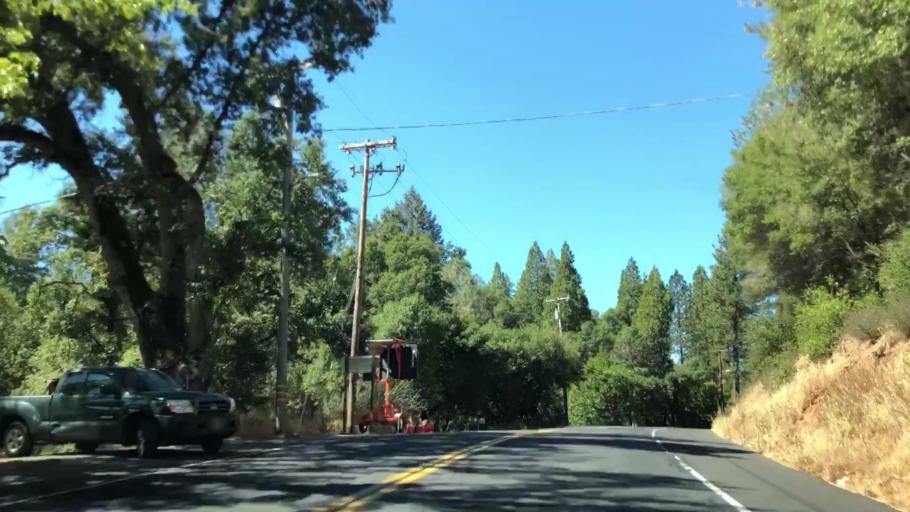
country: US
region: California
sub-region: Tuolumne County
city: Tuolumne City
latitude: 37.8368
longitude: -120.2355
